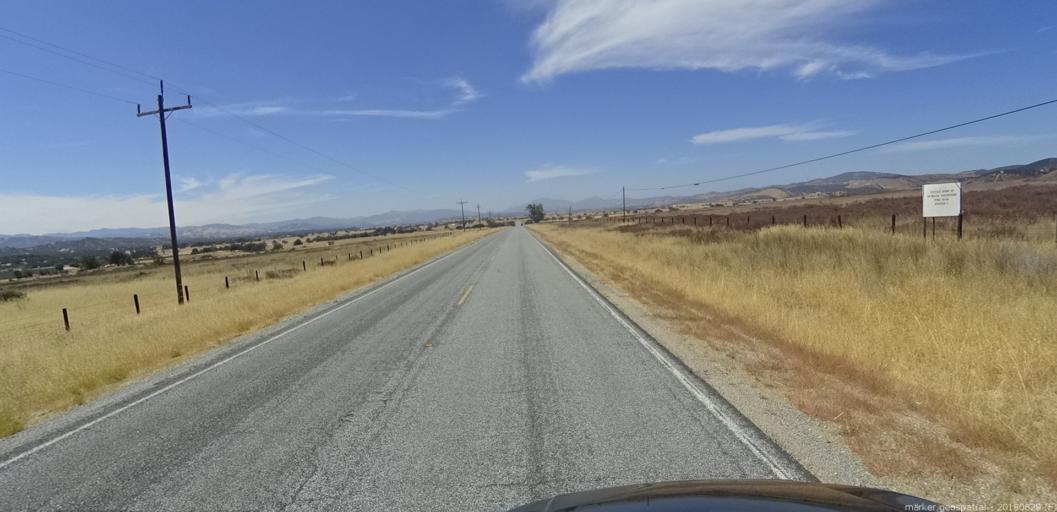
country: US
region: California
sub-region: San Luis Obispo County
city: Lake Nacimiento
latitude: 35.9237
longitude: -121.0398
